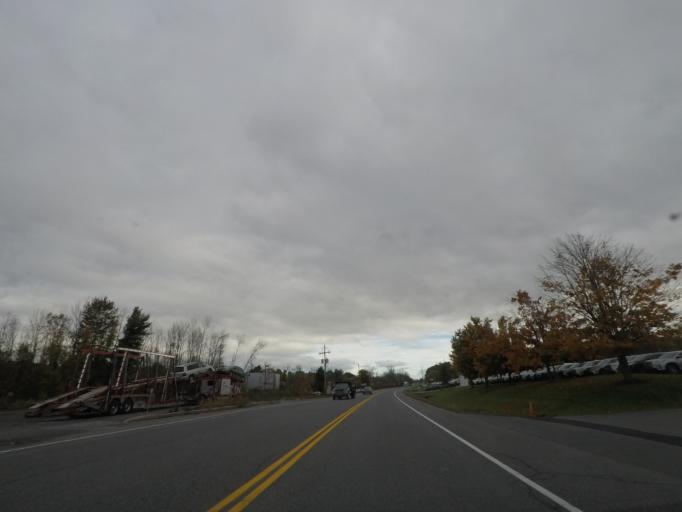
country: US
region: New York
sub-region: Saratoga County
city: Mechanicville
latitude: 42.8699
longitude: -73.7261
